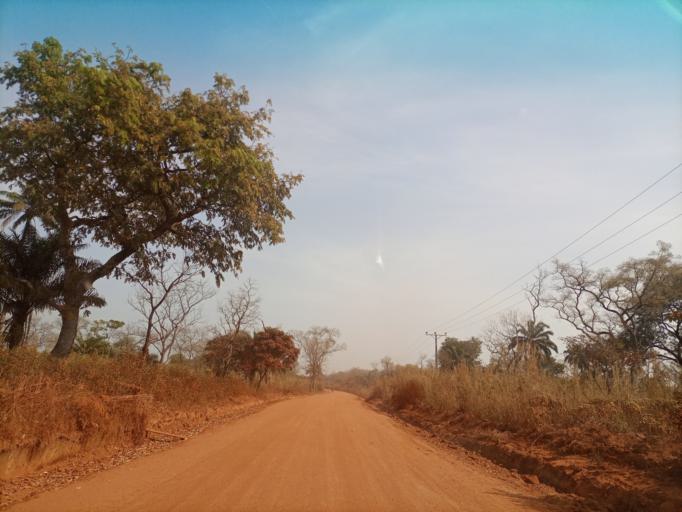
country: NG
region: Enugu
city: Eha Amufu
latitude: 6.6717
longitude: 7.7366
